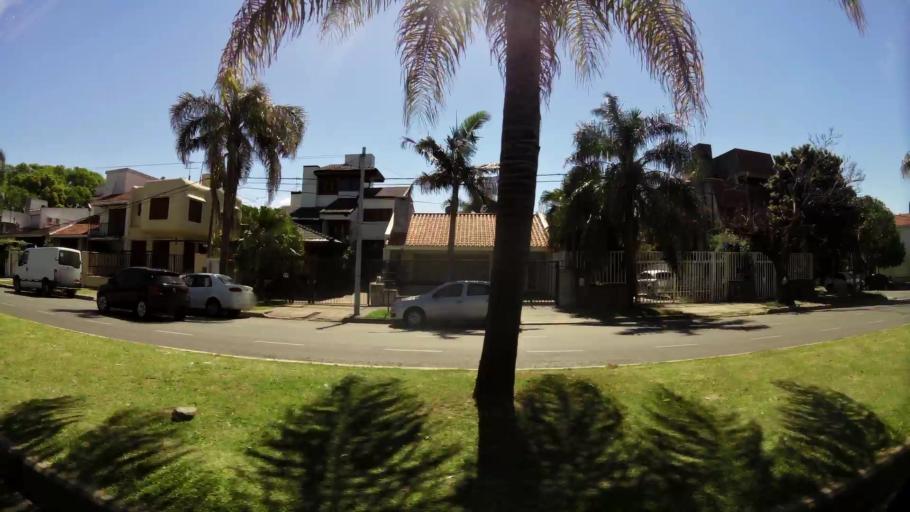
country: AR
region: Santa Fe
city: Santa Fe de la Vera Cruz
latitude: -31.6226
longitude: -60.6785
